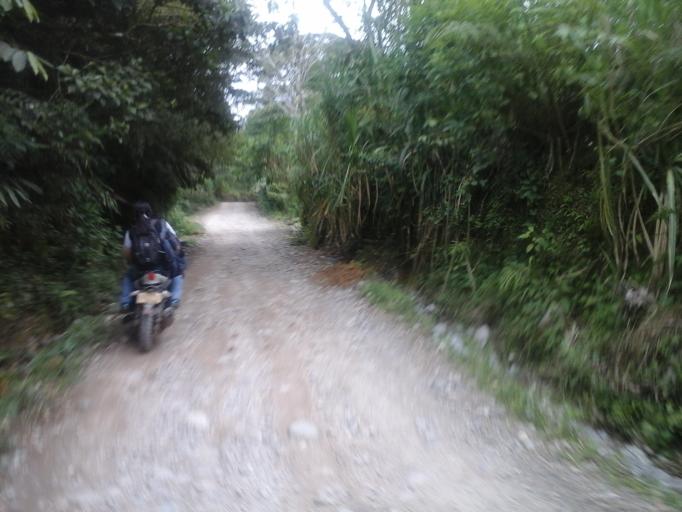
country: CO
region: Putumayo
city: Mocoa
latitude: 1.1829
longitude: -76.6741
